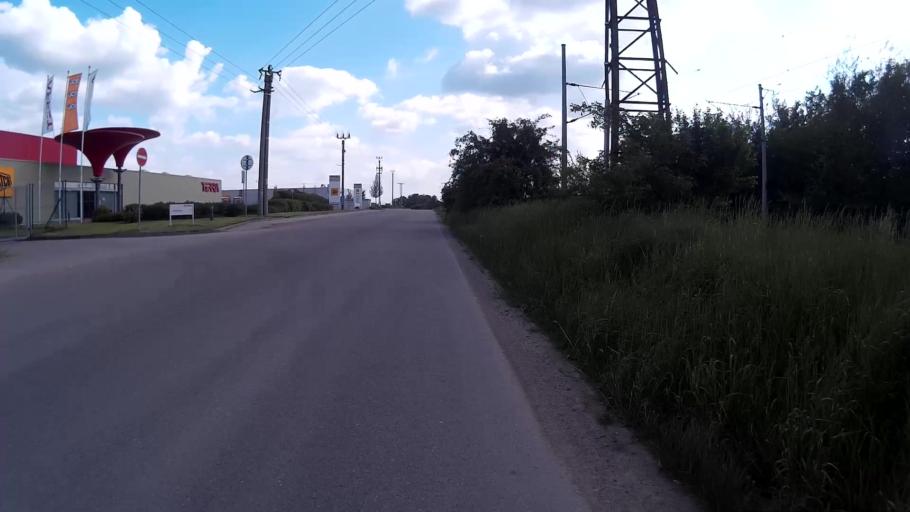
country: CZ
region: South Moravian
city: Modrice
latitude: 49.1149
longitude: 16.6060
